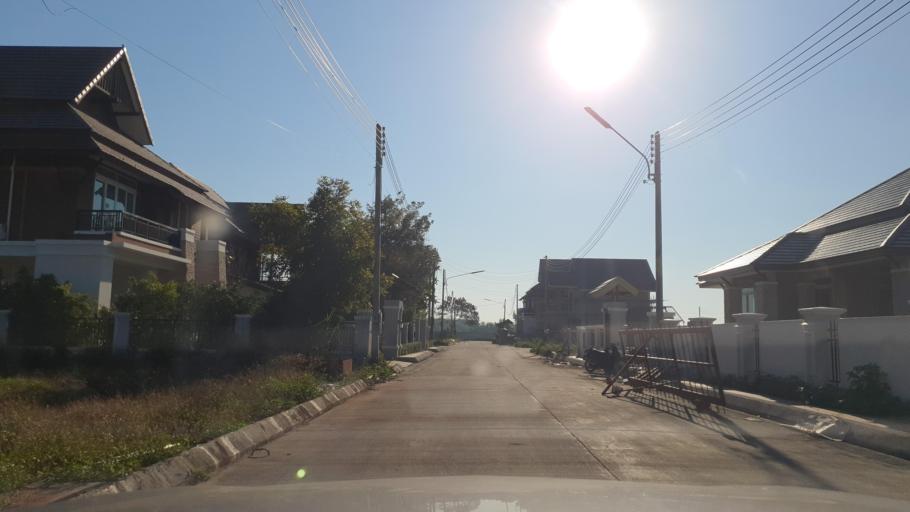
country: TH
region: Chiang Mai
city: Hang Dong
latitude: 18.6975
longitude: 98.9599
